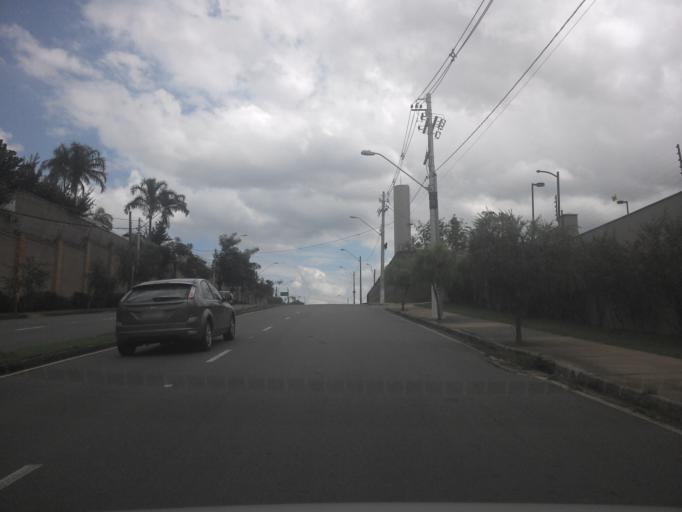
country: BR
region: Sao Paulo
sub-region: Campinas
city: Campinas
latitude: -22.8656
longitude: -47.0290
